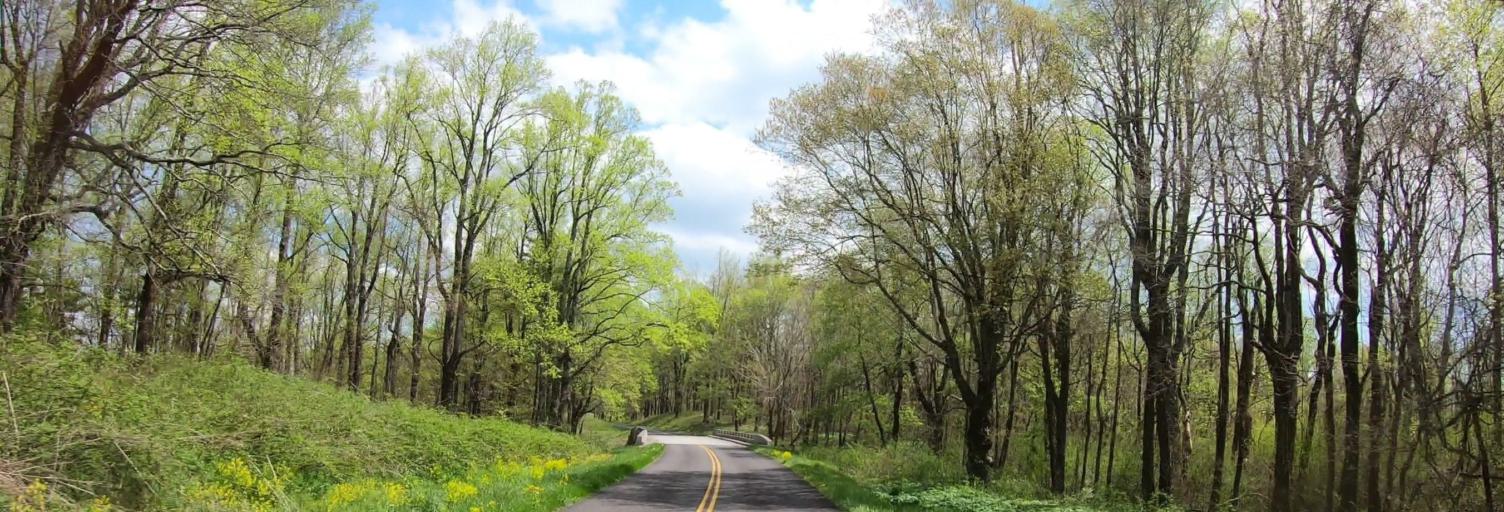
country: US
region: Virginia
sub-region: Carroll County
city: Cana
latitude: 36.6679
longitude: -80.6460
